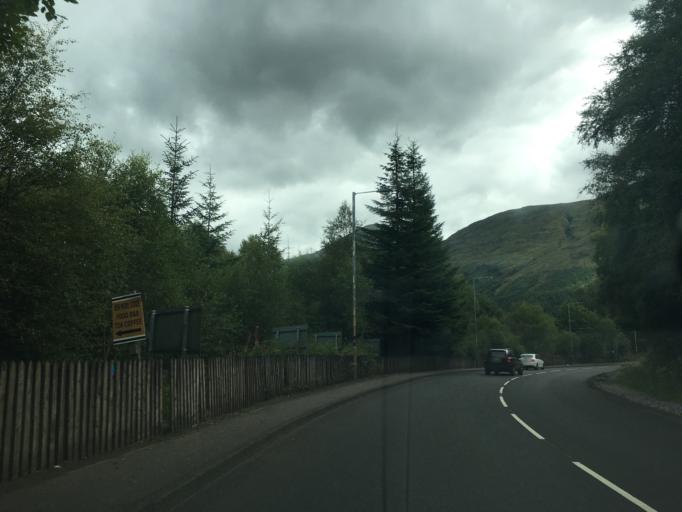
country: GB
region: Scotland
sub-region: Argyll and Bute
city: Garelochhead
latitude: 56.3922
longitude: -4.6134
